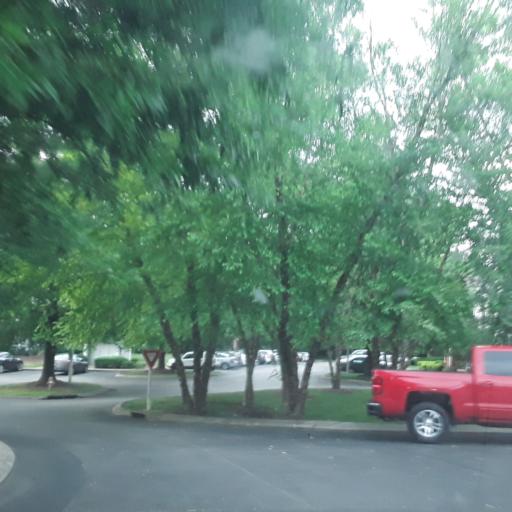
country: US
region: Tennessee
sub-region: Wilson County
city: Green Hill
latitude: 36.1661
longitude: -86.6044
